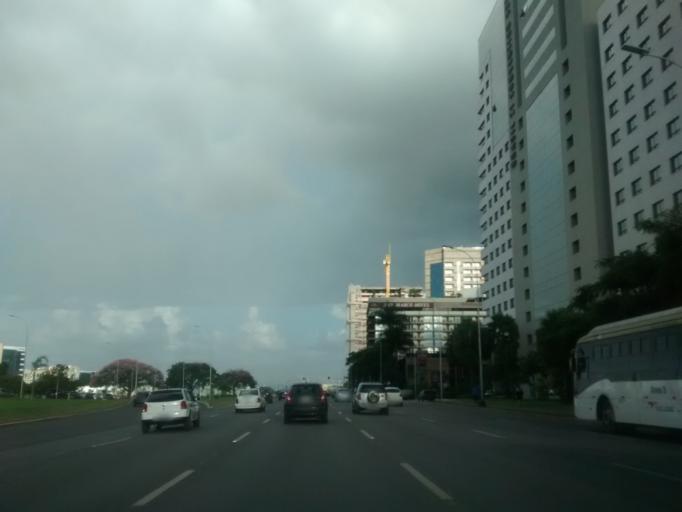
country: BR
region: Federal District
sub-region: Brasilia
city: Brasilia
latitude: -15.7921
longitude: -47.8936
